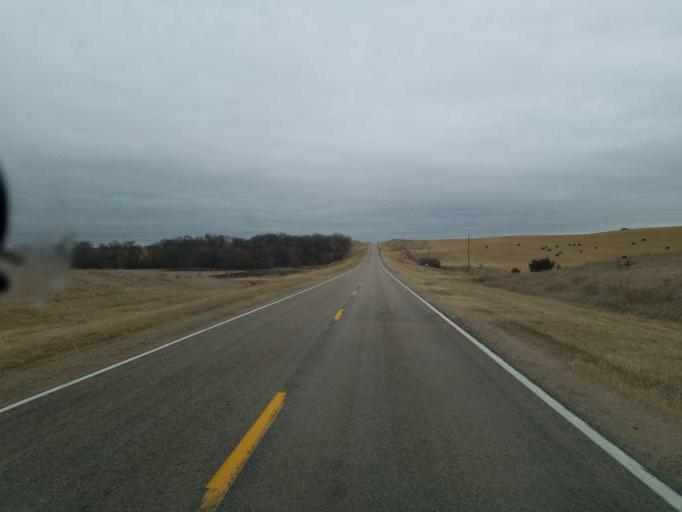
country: US
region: Nebraska
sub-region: Knox County
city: Bloomfield
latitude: 42.6127
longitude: -97.4957
